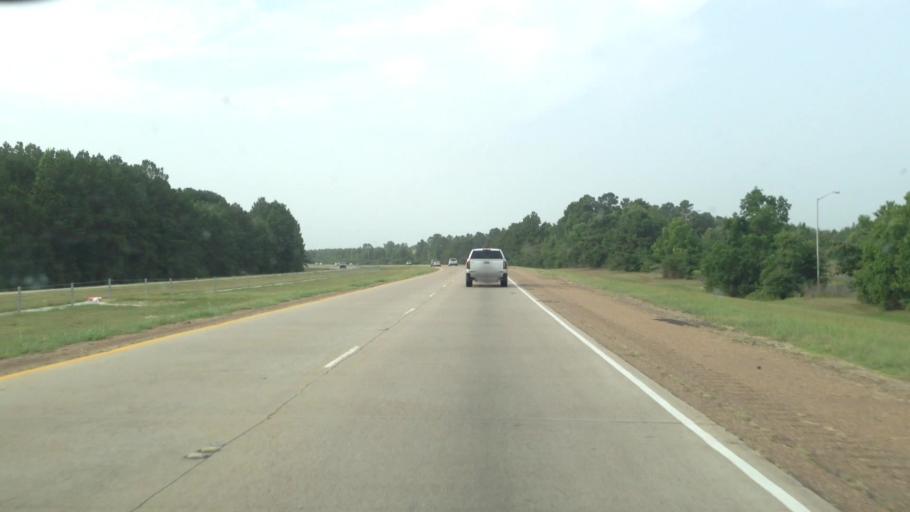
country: US
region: Louisiana
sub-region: Caddo Parish
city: Shreveport
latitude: 32.4310
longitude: -93.8399
